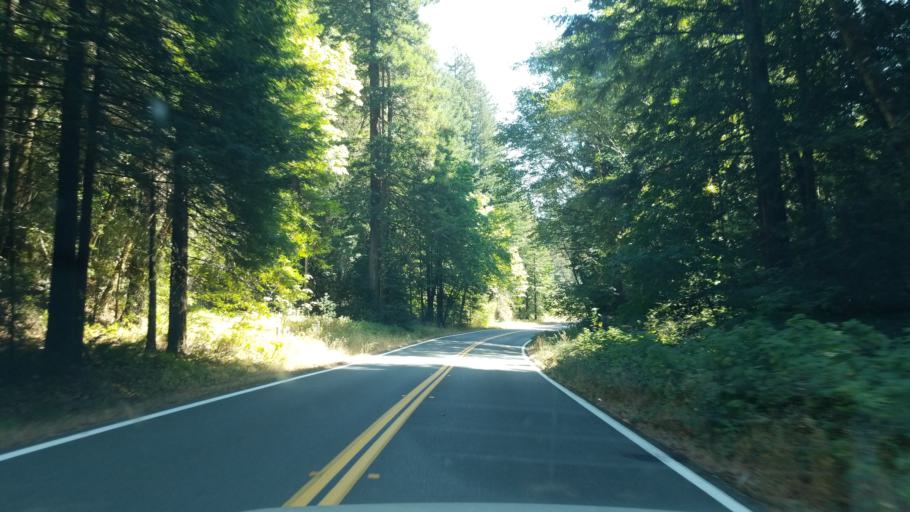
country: US
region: California
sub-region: Humboldt County
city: Redway
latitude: 40.3287
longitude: -123.9264
